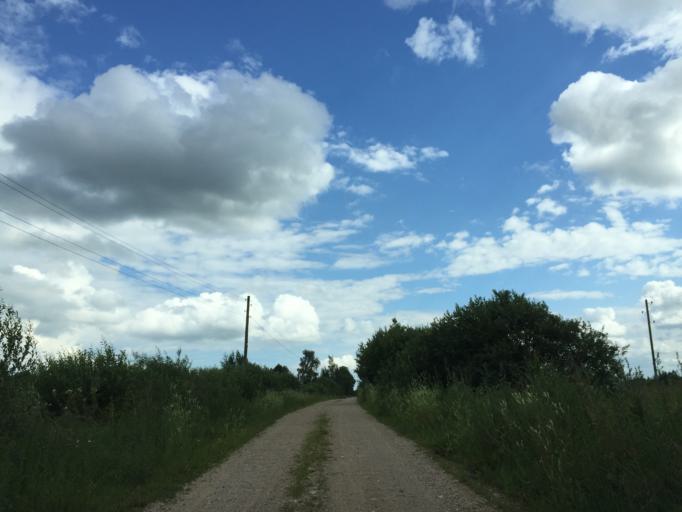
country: LV
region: Ogre
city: Jumprava
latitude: 56.8422
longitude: 25.0529
